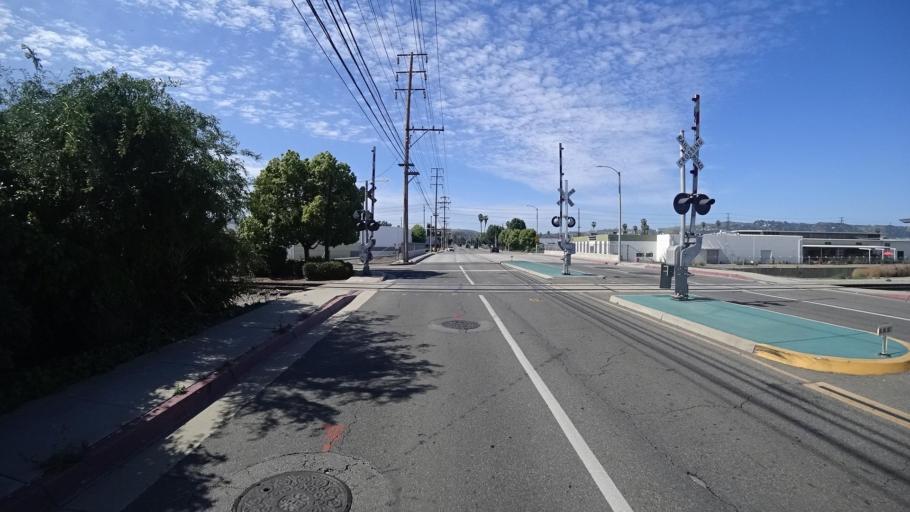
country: US
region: California
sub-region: Los Angeles County
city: La Puente
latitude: 34.0131
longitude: -117.9540
